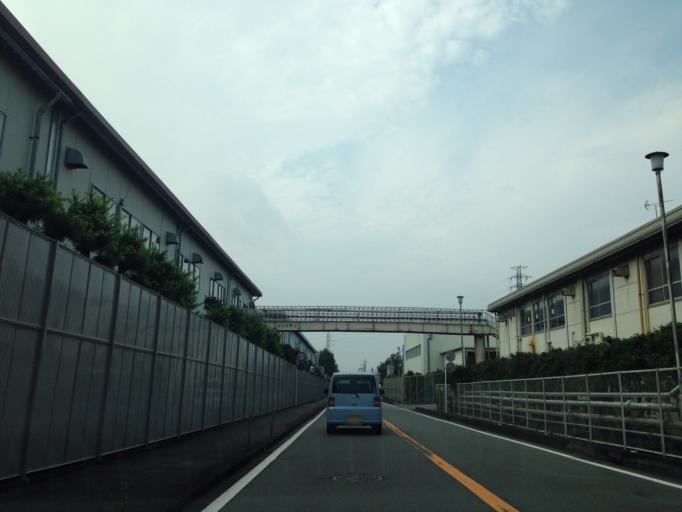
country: JP
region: Shizuoka
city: Mishima
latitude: 35.1615
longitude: 138.9075
